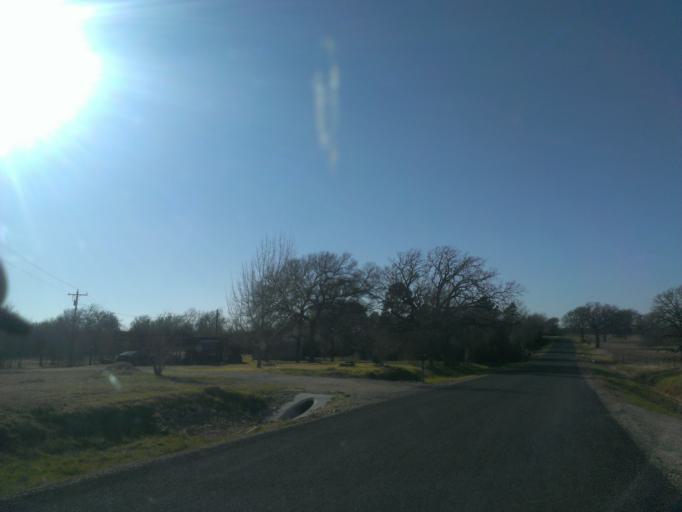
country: US
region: Texas
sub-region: Milam County
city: Thorndale
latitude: 30.4816
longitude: -97.2452
